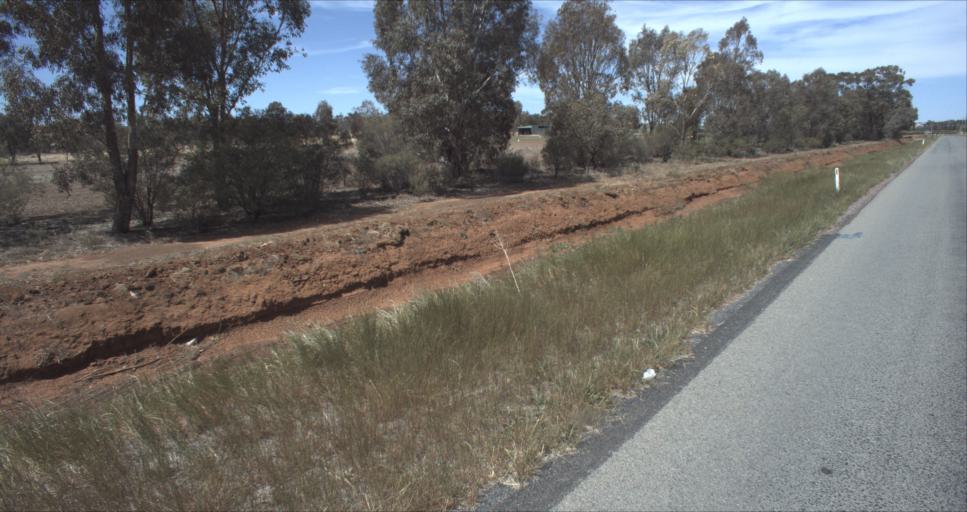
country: AU
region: New South Wales
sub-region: Leeton
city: Leeton
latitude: -34.5584
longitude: 146.4533
